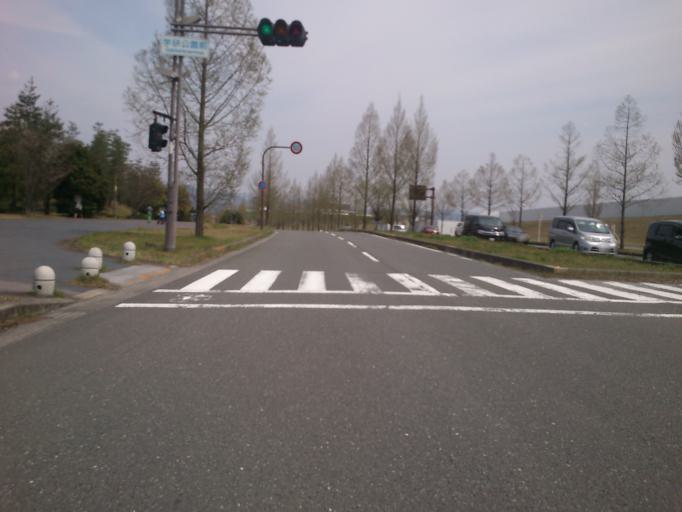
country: JP
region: Nara
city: Nara-shi
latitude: 34.7450
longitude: 135.7752
